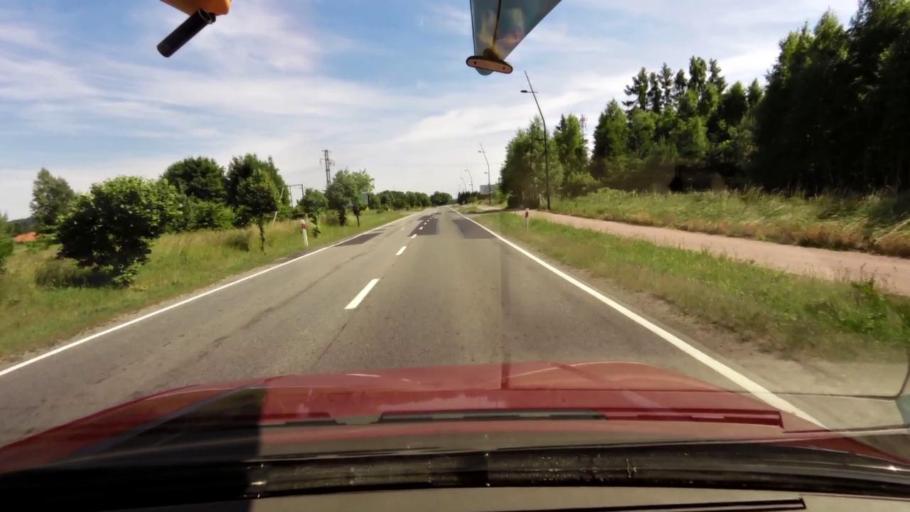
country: PL
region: Pomeranian Voivodeship
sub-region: Powiat slupski
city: Kobylnica
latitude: 54.4322
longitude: 17.0026
